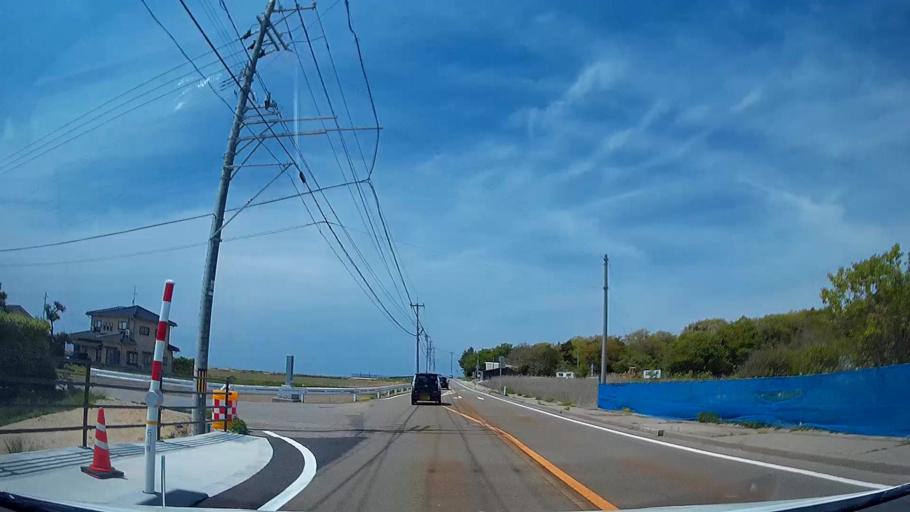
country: JP
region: Ishikawa
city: Hakui
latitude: 36.9279
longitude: 136.7583
